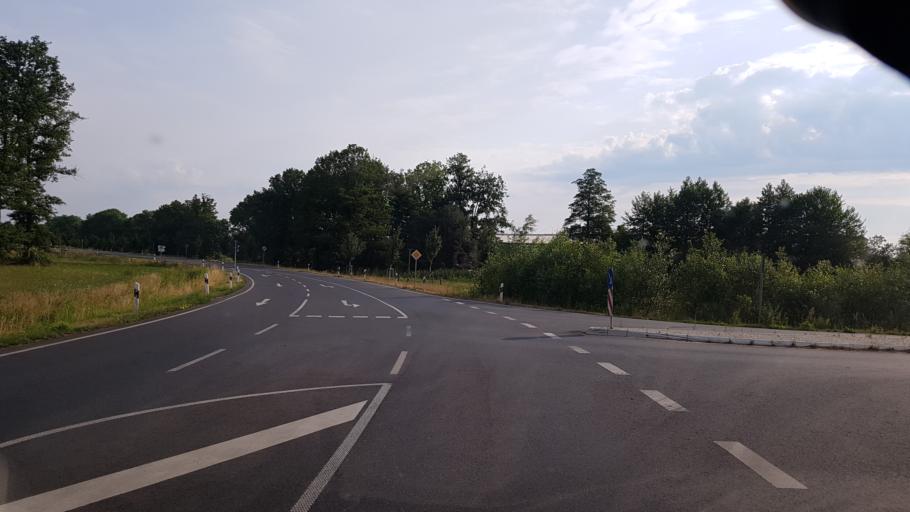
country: DE
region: Brandenburg
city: Golssen
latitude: 51.9717
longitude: 13.5708
